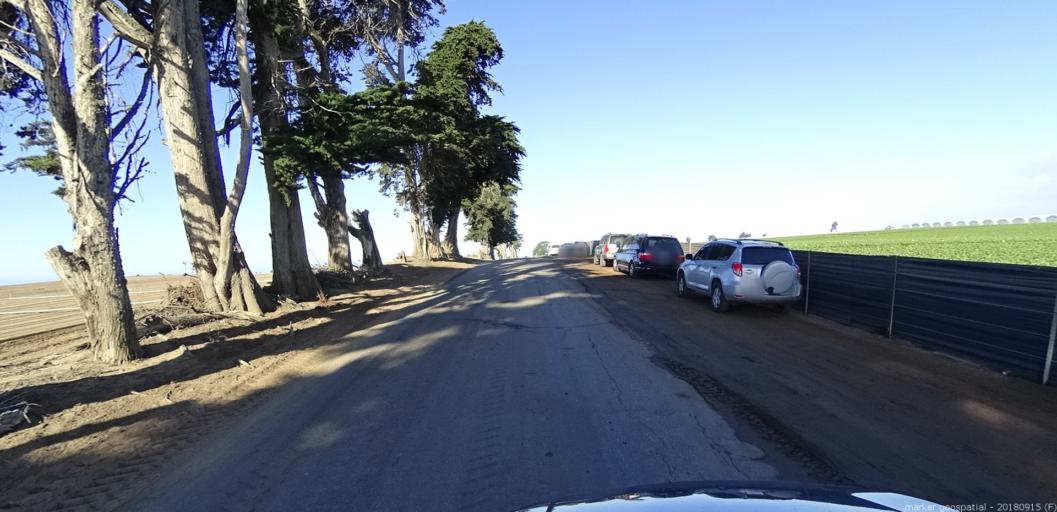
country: US
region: California
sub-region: Monterey County
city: Elkhorn
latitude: 36.8271
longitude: -121.7815
